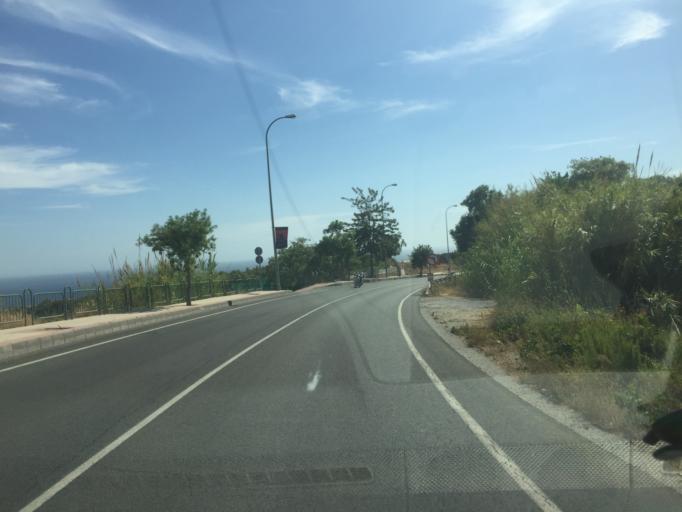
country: ES
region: Andalusia
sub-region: Provincia de Malaga
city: Nerja
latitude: 36.7580
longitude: -3.8475
